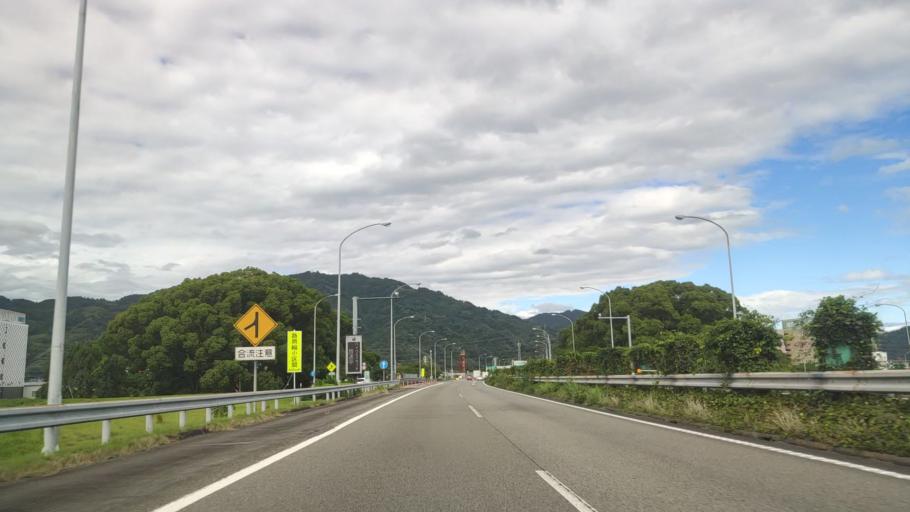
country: JP
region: Shizuoka
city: Yaizu
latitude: 34.8804
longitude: 138.2981
